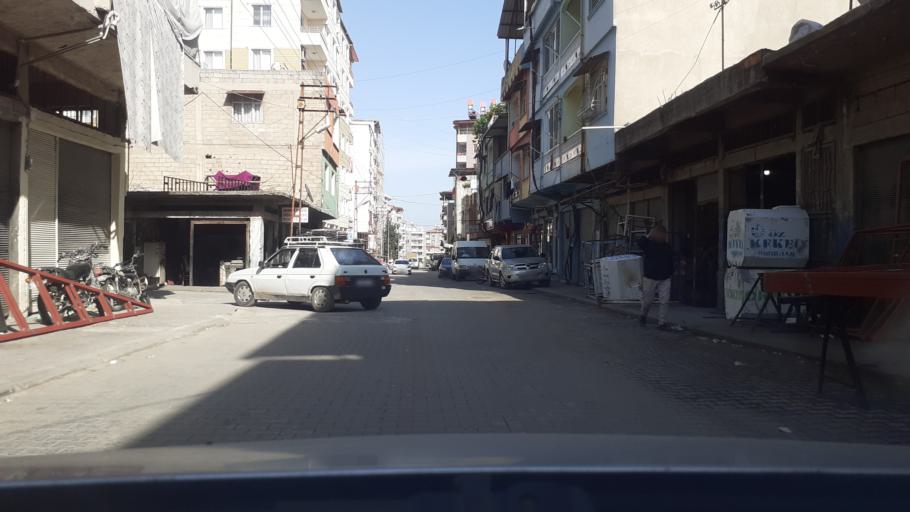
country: TR
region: Hatay
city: Kirikhan
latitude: 36.4969
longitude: 36.3613
